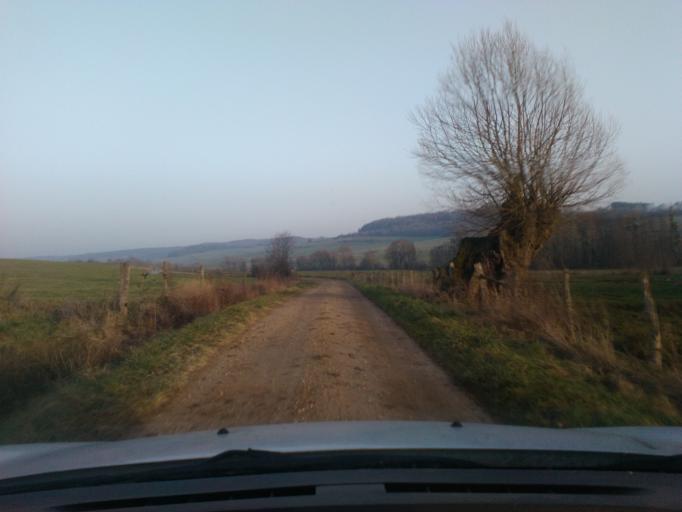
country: FR
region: Lorraine
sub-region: Departement des Vosges
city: Vittel
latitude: 48.2612
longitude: 6.0144
